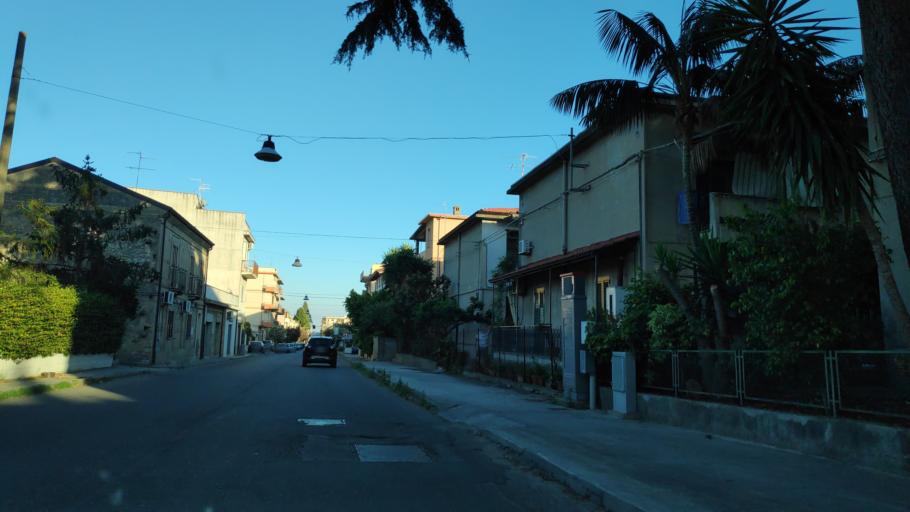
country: IT
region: Calabria
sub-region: Provincia di Reggio Calabria
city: Locri
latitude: 38.2378
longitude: 16.2572
